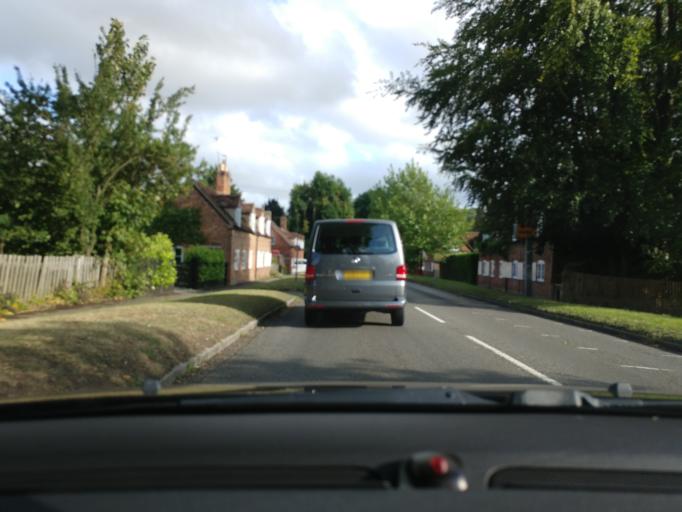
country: GB
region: England
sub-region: Oxfordshire
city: Radley
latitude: 51.6886
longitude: -1.2014
